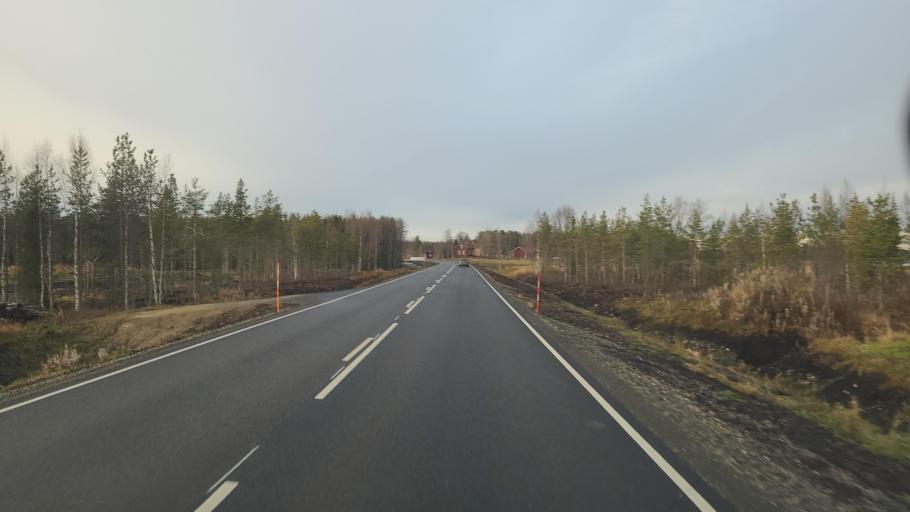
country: FI
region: Lapland
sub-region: Tunturi-Lappi
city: Kittilae
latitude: 67.8760
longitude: 24.8881
